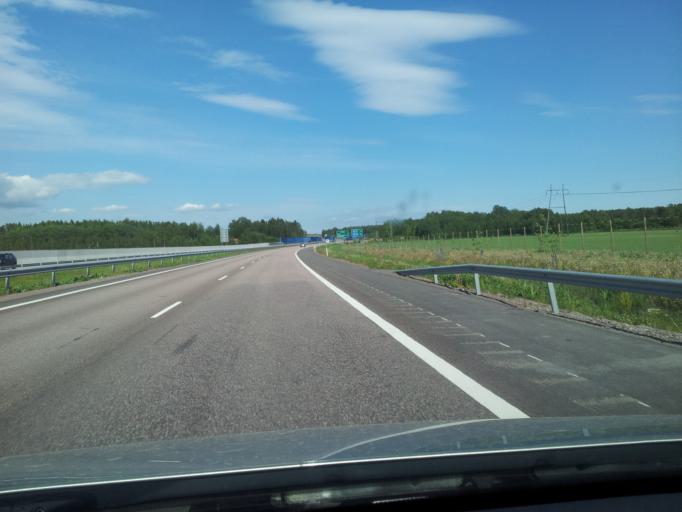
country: FI
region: Uusimaa
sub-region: Loviisa
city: Lovisa
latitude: 60.4651
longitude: 26.2115
